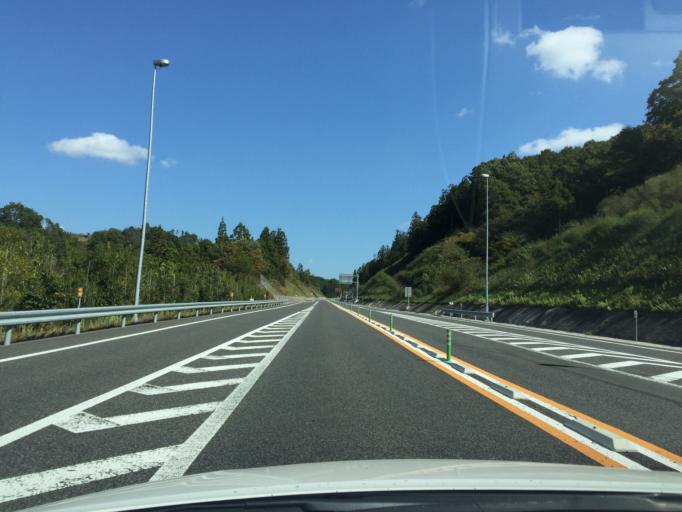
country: JP
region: Fukushima
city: Ishikawa
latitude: 37.2072
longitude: 140.5263
